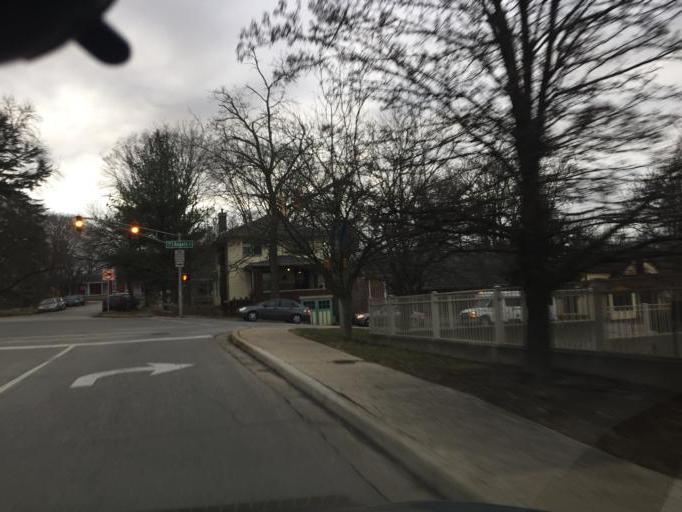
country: US
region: Indiana
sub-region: Monroe County
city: Bloomington
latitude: 39.1646
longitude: -86.5383
